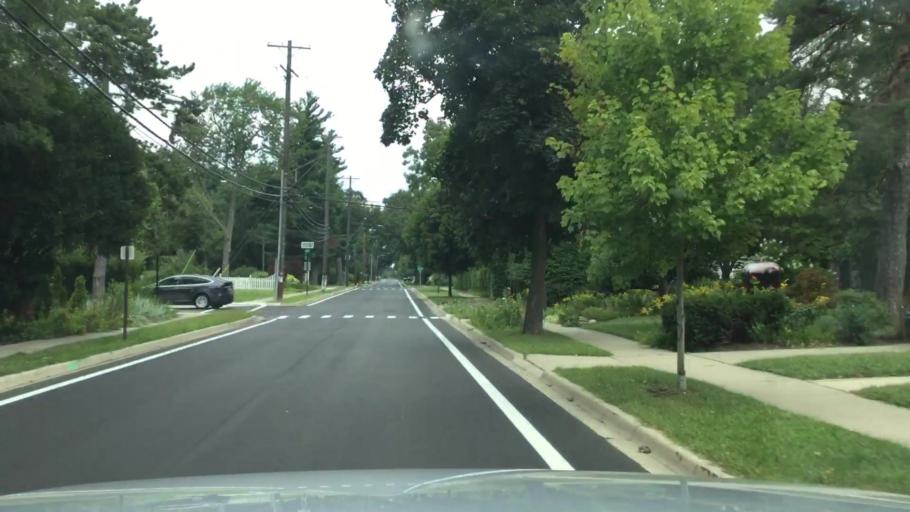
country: US
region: Michigan
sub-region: Oakland County
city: Pleasant Ridge
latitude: 42.4692
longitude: -83.1482
